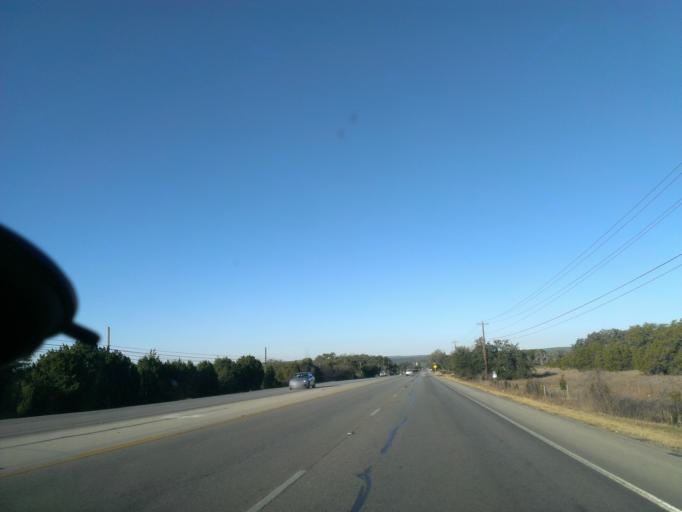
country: US
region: Texas
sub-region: Hays County
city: Dripping Springs
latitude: 30.1918
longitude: -98.0753
